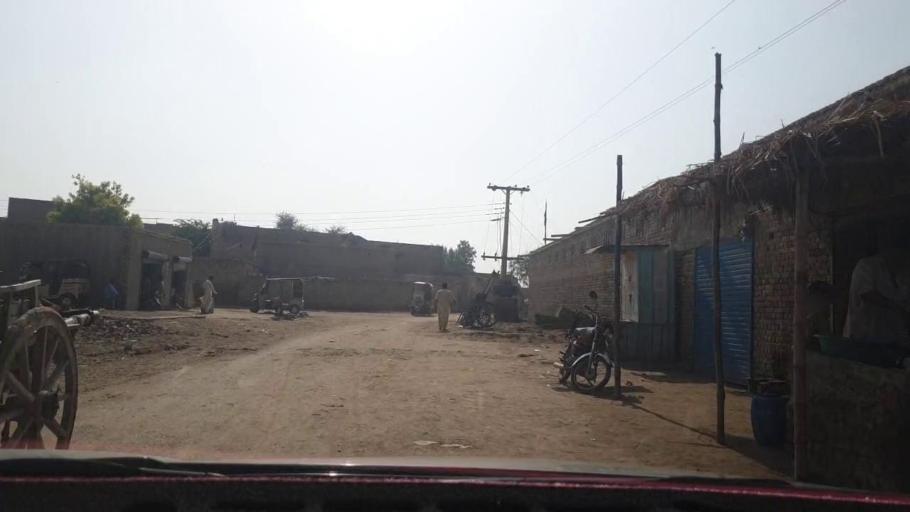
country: PK
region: Sindh
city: Nasirabad
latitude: 27.4390
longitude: 67.9543
